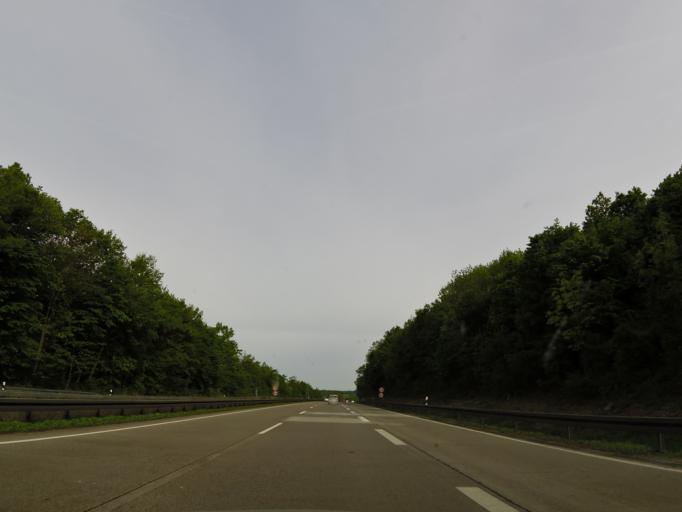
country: DE
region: Lower Saxony
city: Holle
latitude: 52.1055
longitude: 10.1419
